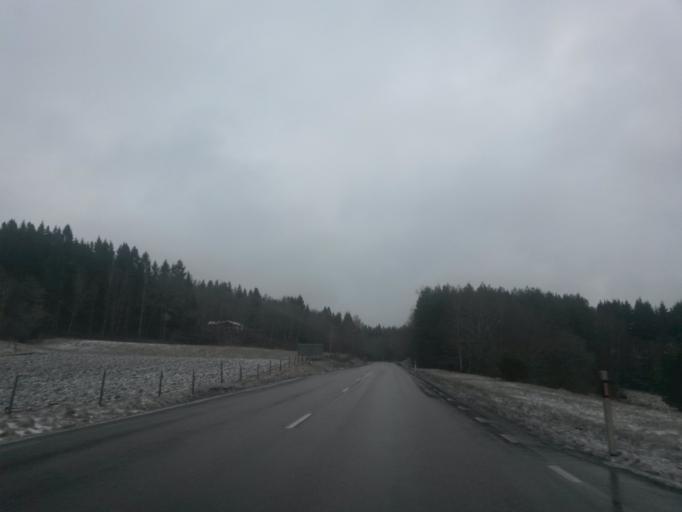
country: SE
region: Vaestra Goetaland
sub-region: Vargarda Kommun
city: Jonstorp
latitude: 58.0674
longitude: 12.6841
